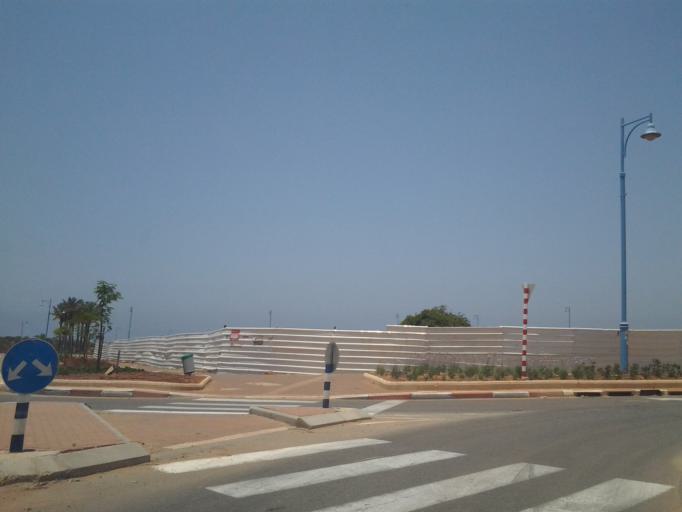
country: IL
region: Haifa
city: Hadera
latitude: 32.4293
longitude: 34.8820
